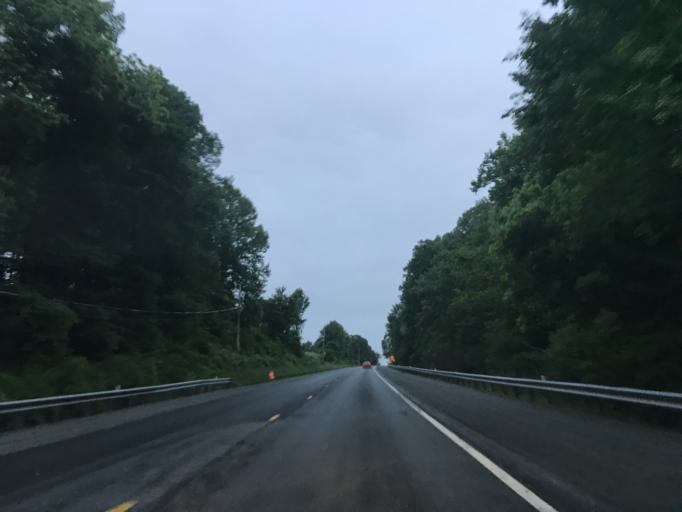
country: US
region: Maryland
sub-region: Frederick County
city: Linganore
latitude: 39.4167
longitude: -77.2538
